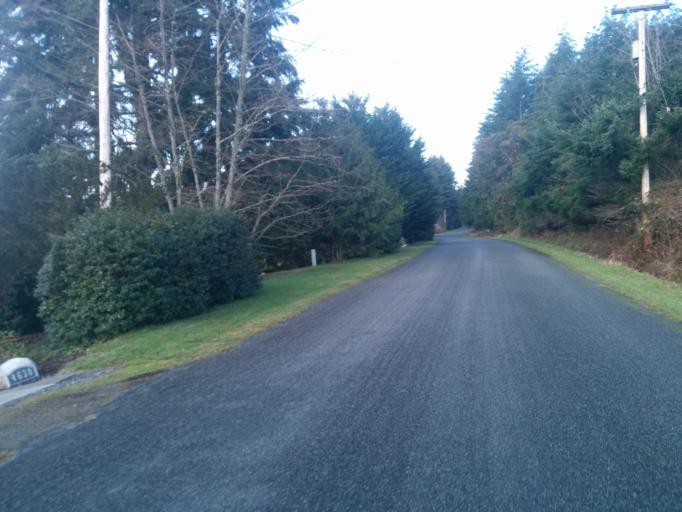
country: US
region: Washington
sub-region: Island County
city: Freeland
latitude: 48.0430
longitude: -122.4977
